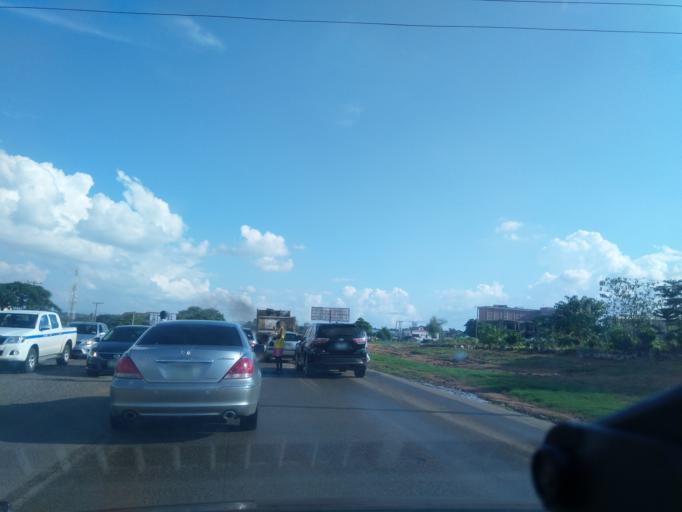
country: NG
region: Abuja Federal Capital Territory
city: Abuja
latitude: 9.0574
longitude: 7.4107
